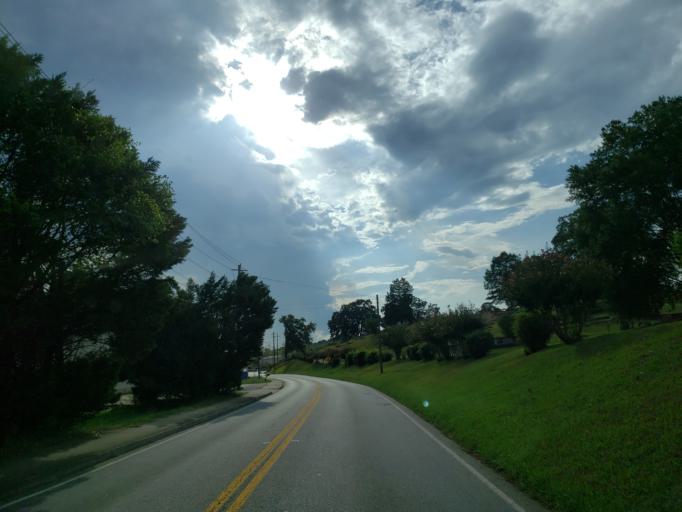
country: US
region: Georgia
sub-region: Bartow County
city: Cartersville
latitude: 34.1756
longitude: -84.8078
